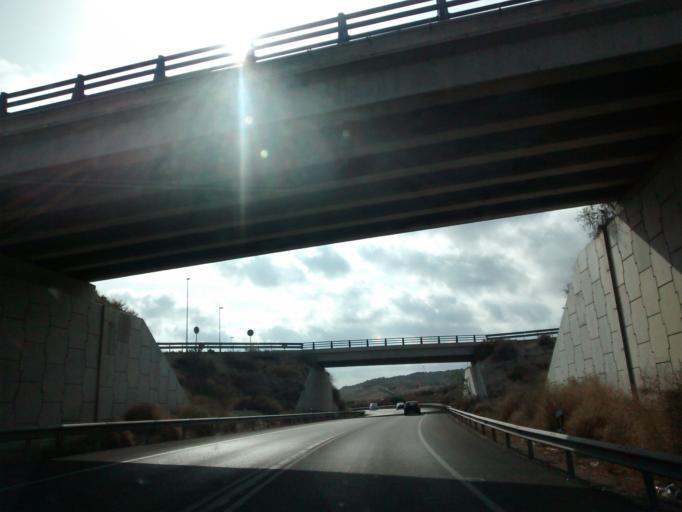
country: ES
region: Valencia
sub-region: Provincia de Alicante
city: el Campello
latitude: 38.4437
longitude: -0.3883
